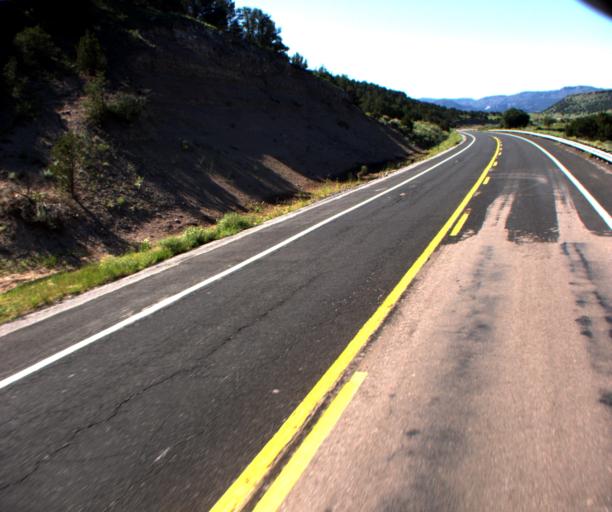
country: US
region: Arizona
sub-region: Apache County
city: Eagar
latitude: 34.0502
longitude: -109.1876
